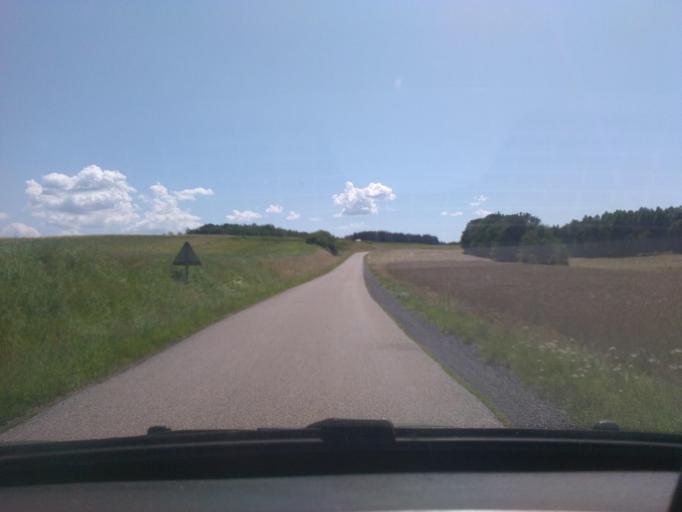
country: FR
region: Lorraine
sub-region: Departement des Vosges
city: Etival-Clairefontaine
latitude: 48.3511
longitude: 6.8642
